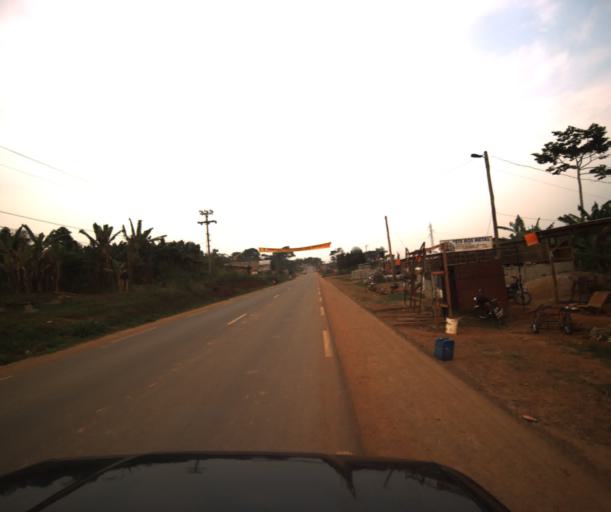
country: CM
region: Centre
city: Mbankomo
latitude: 3.8024
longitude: 11.4547
